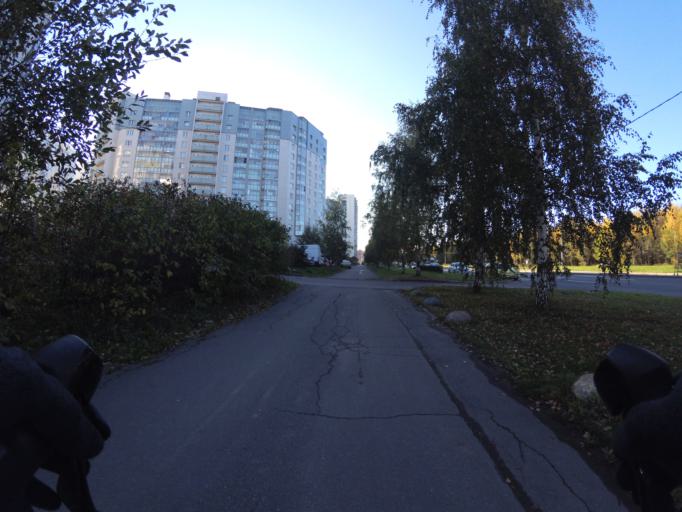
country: RU
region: Leningrad
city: Untolovo
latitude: 59.9969
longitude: 30.1932
